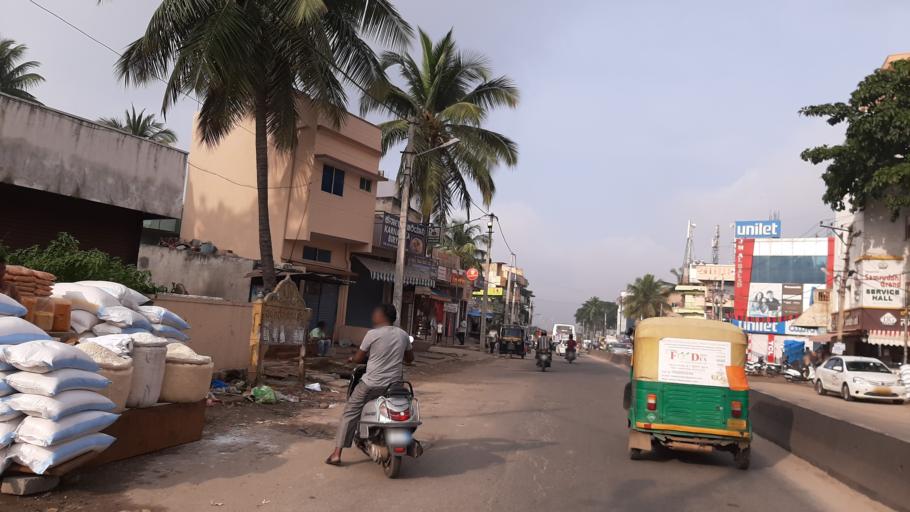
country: IN
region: Karnataka
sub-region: Bangalore Urban
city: Bangalore
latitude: 12.9899
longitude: 77.5024
